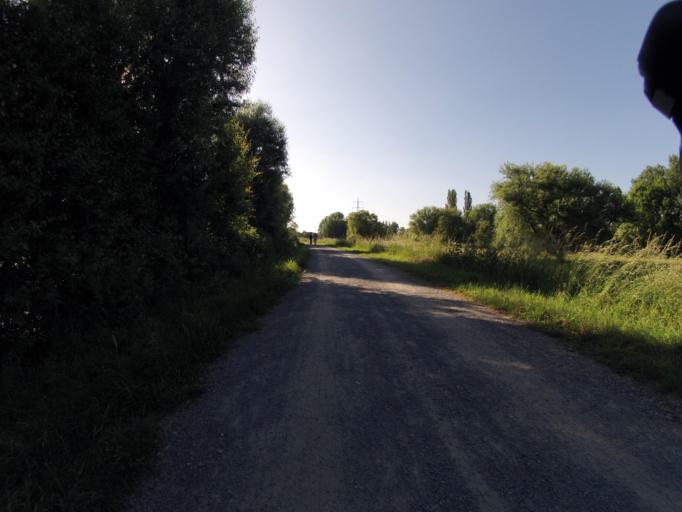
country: DE
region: Lower Saxony
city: Schuttorf
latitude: 52.3194
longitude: 7.2317
